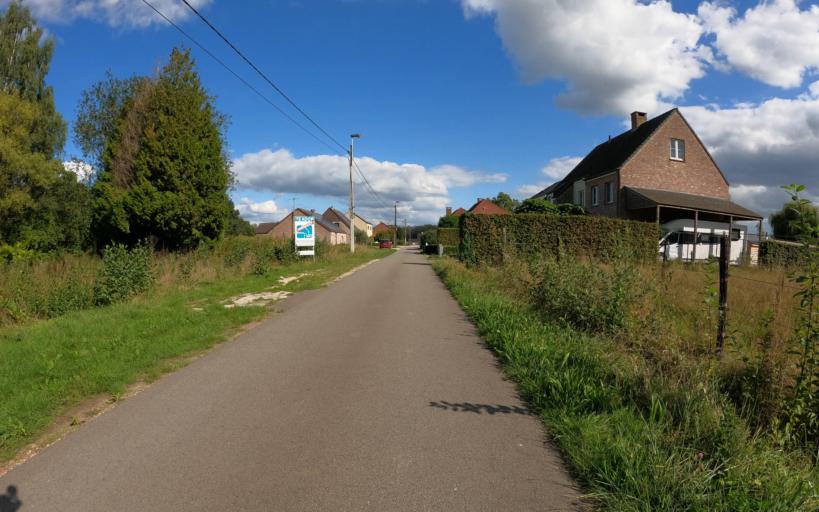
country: BE
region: Flanders
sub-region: Provincie Antwerpen
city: Ranst
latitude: 51.1976
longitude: 4.5735
